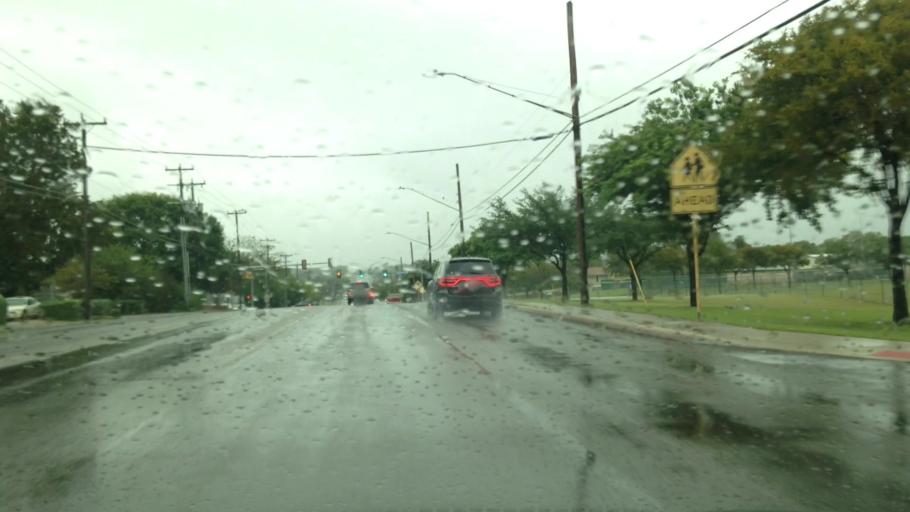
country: US
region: Texas
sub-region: Bexar County
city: Live Oak
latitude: 29.5739
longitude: -98.3697
